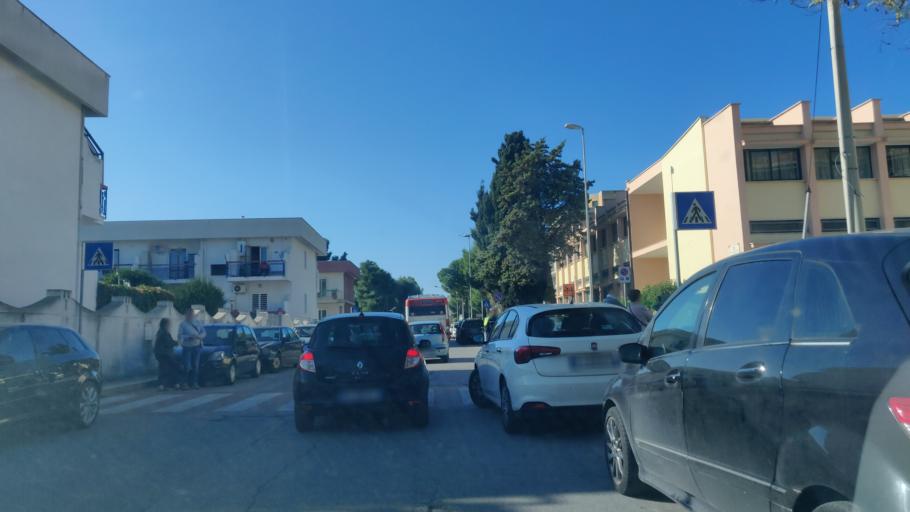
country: IT
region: Apulia
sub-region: Provincia di Bari
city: San Paolo
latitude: 41.1362
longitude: 16.8210
